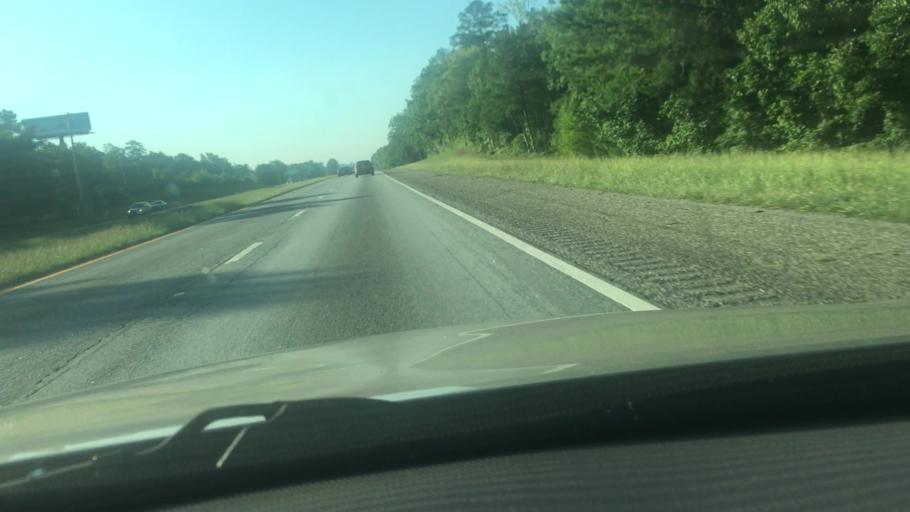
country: US
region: South Carolina
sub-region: Lexington County
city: Irmo
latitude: 34.1171
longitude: -81.1938
